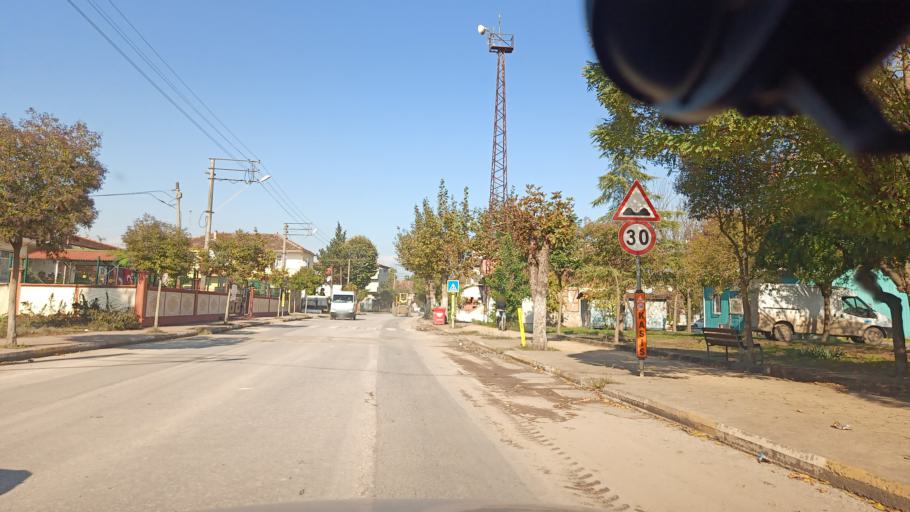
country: TR
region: Sakarya
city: Sogutlu
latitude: 40.9014
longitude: 30.4704
